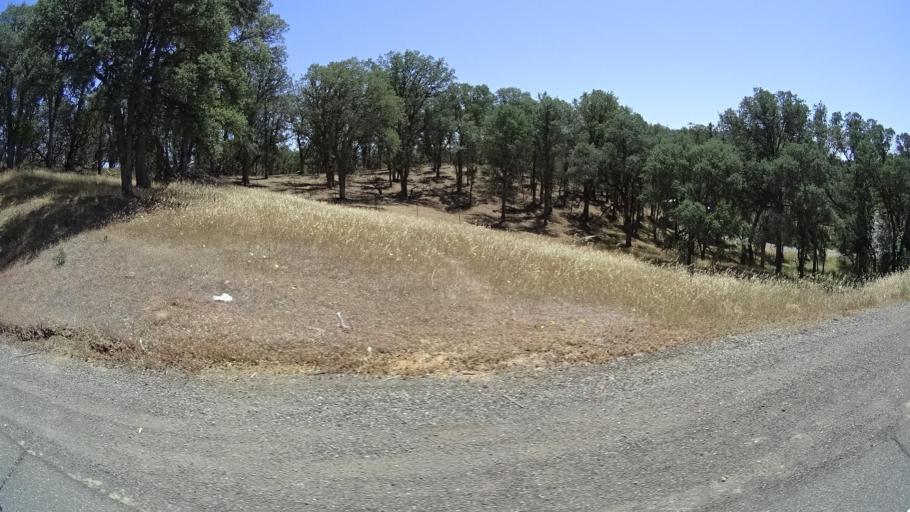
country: US
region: California
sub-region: Lake County
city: Lower Lake
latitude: 38.8836
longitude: -122.6057
